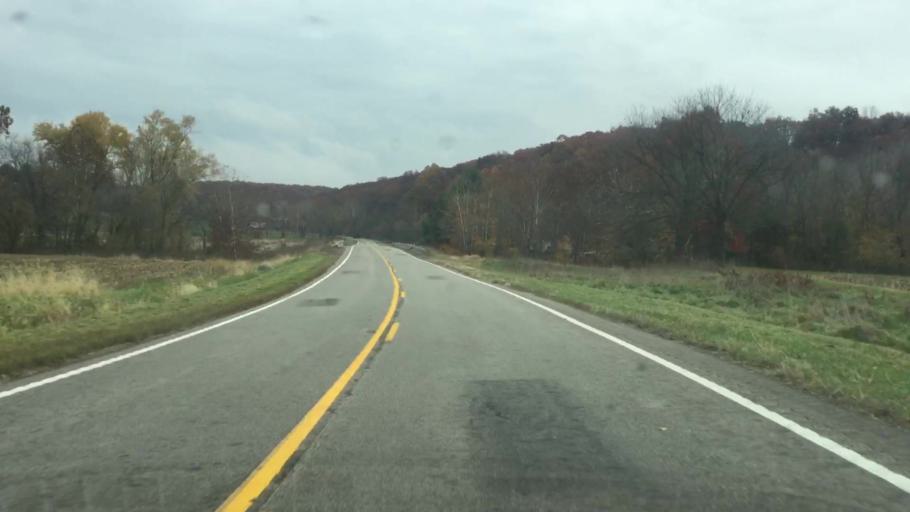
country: US
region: Missouri
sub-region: Gasconade County
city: Hermann
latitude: 38.7174
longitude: -91.6614
